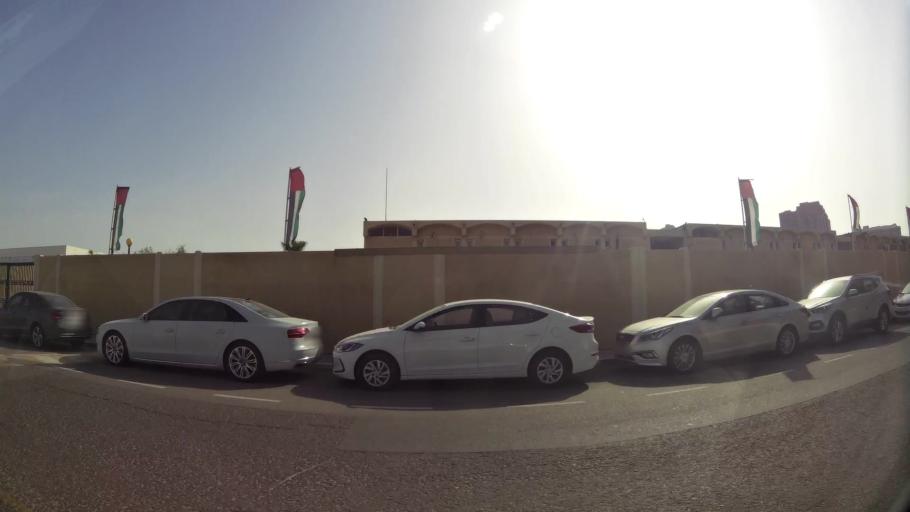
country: AE
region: Ash Shariqah
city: Sharjah
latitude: 25.2872
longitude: 55.3529
